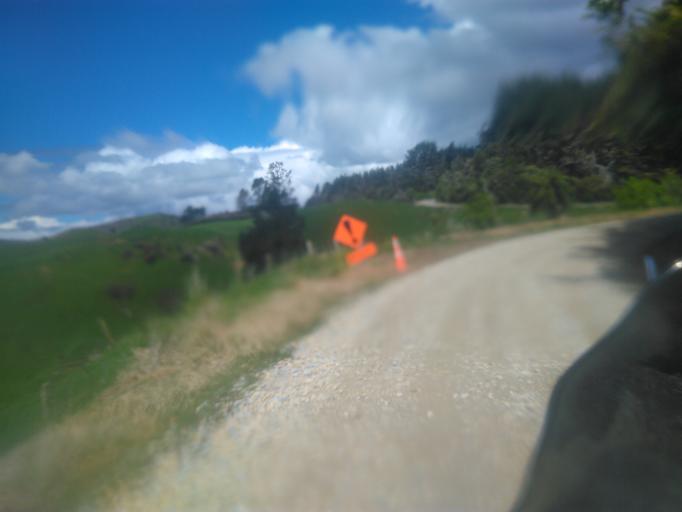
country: NZ
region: Hawke's Bay
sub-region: Wairoa District
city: Wairoa
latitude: -38.7736
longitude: 177.6060
